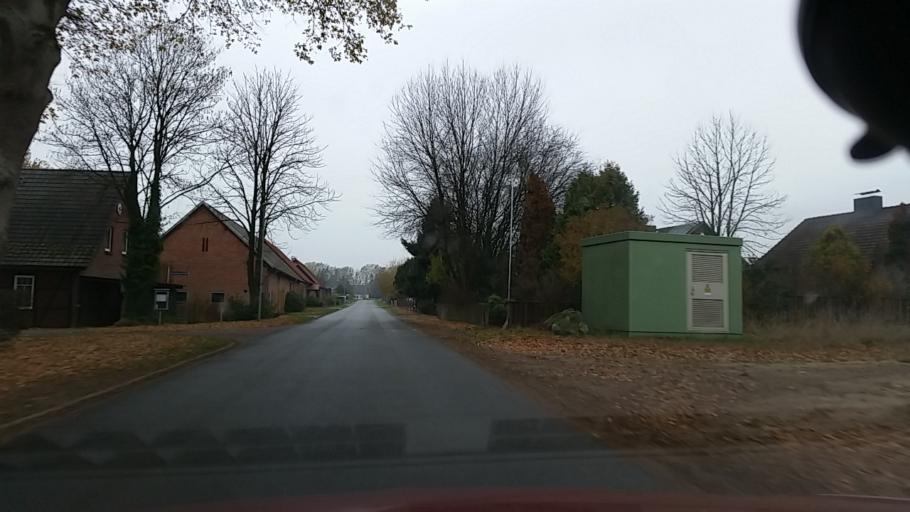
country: DE
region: Lower Saxony
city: Obernholz
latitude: 52.7670
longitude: 10.5954
